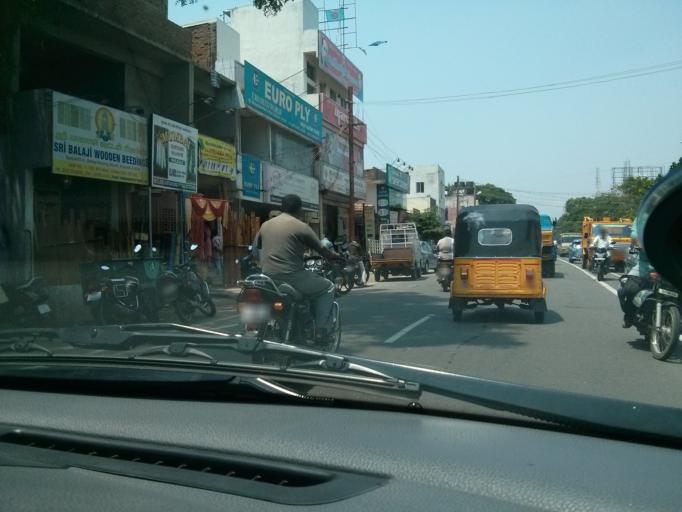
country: IN
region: Tamil Nadu
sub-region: Coimbatore
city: Coimbatore
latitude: 11.0128
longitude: 76.9549
